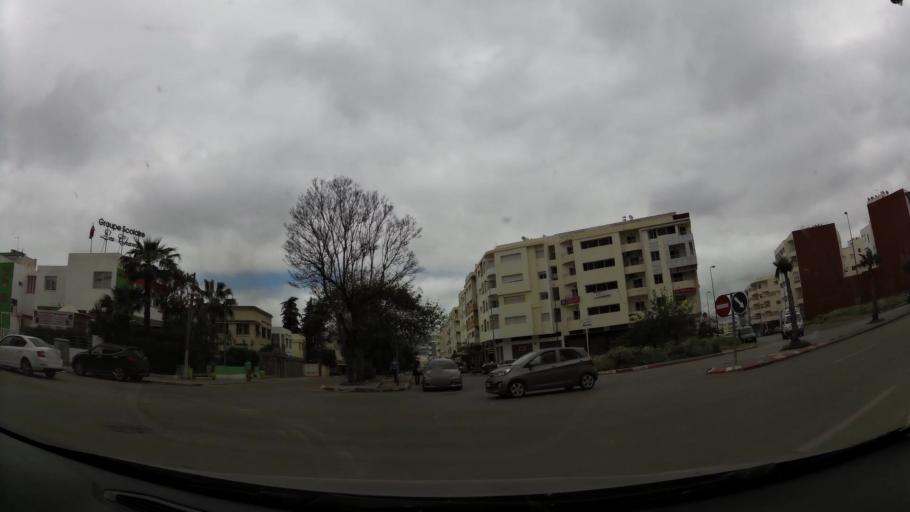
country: MA
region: Fes-Boulemane
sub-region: Fes
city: Fes
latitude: 34.0360
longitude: -5.0150
